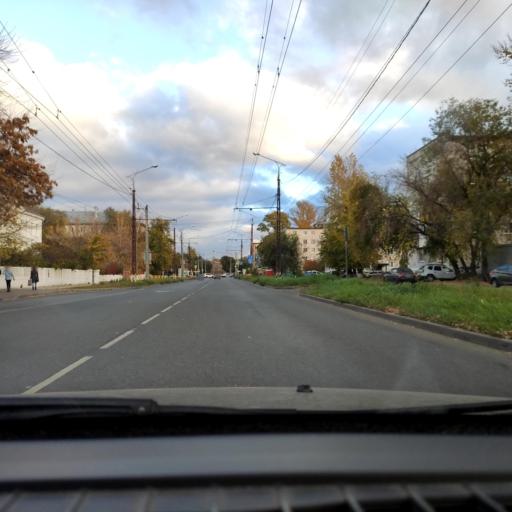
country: RU
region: Samara
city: Tol'yatti
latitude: 53.5215
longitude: 49.4239
